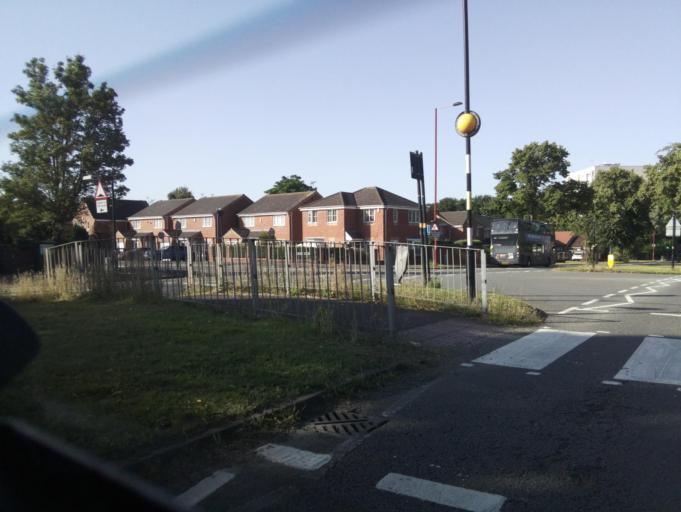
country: GB
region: England
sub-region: City and Borough of Birmingham
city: Sutton Coldfield
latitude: 52.5207
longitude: -1.8108
